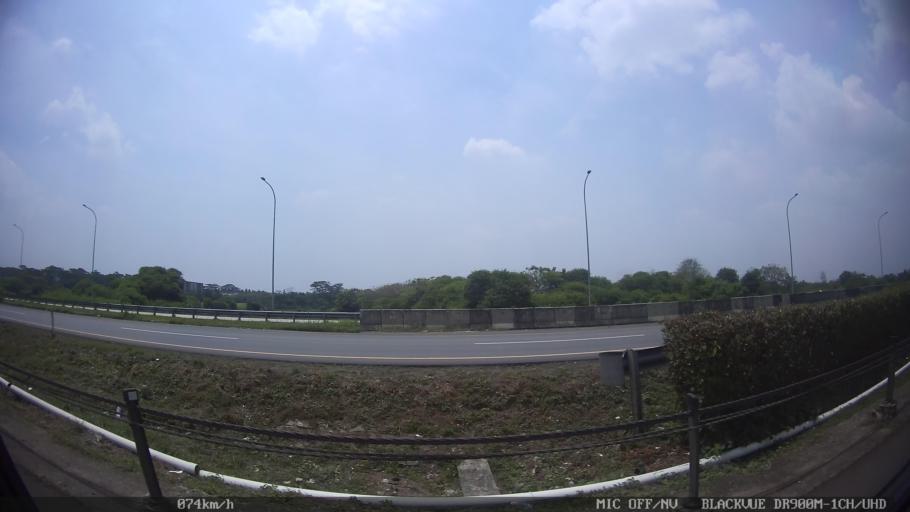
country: ID
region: Banten
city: Serang
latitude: -6.1387
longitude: 106.2499
